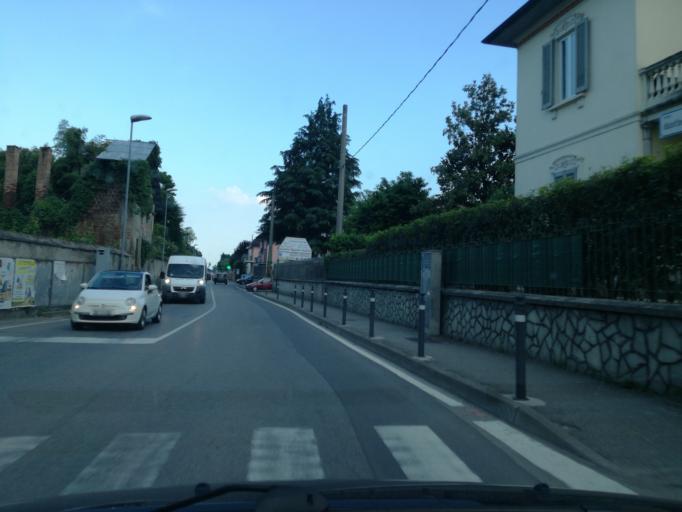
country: IT
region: Lombardy
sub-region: Provincia di Monza e Brianza
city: Porto d'Adda
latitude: 45.6459
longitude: 9.4644
